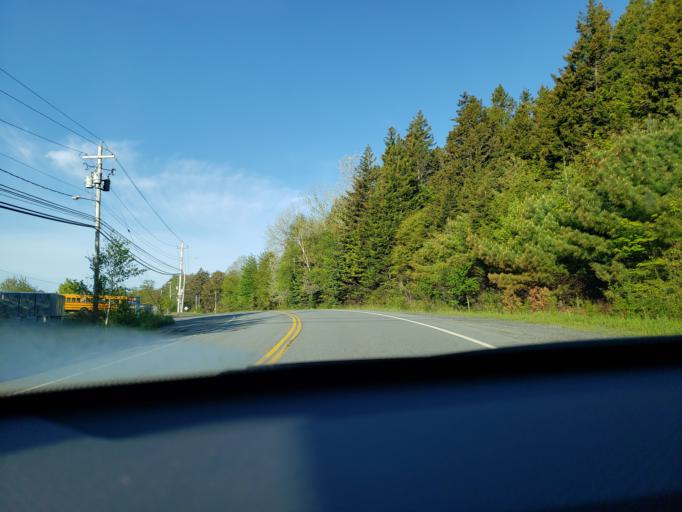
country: CA
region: Nova Scotia
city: Cole Harbour
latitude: 44.7401
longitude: -63.3856
